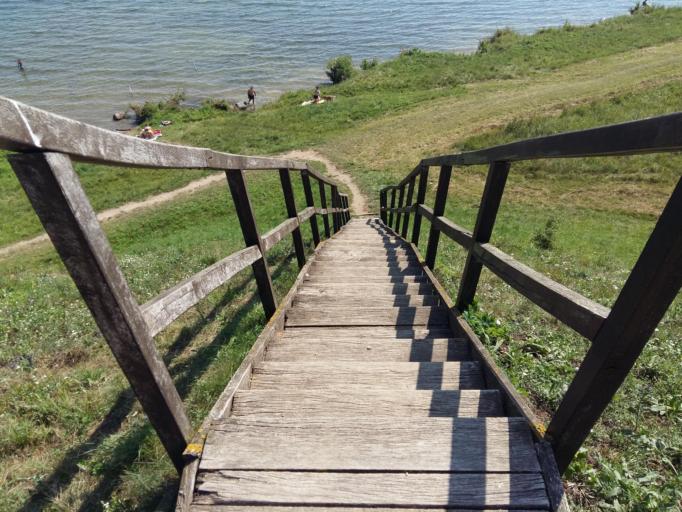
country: LT
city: Simnas
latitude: 54.3132
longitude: 23.6549
